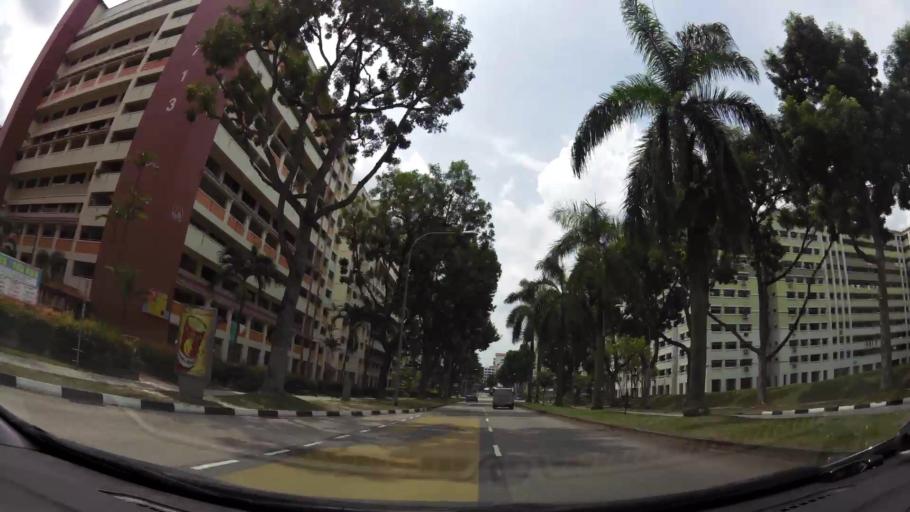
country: MY
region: Johor
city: Johor Bahru
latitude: 1.3441
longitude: 103.6959
